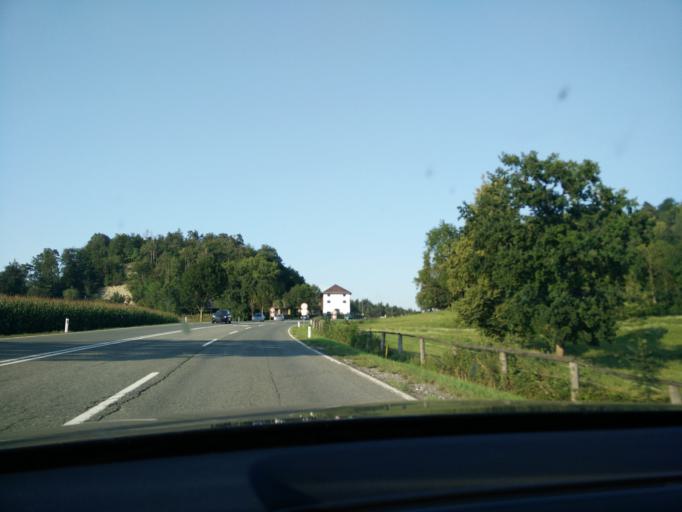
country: AT
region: Carinthia
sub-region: Politischer Bezirk Klagenfurt Land
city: Kottmannsdorf
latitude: 46.5484
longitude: 14.2585
